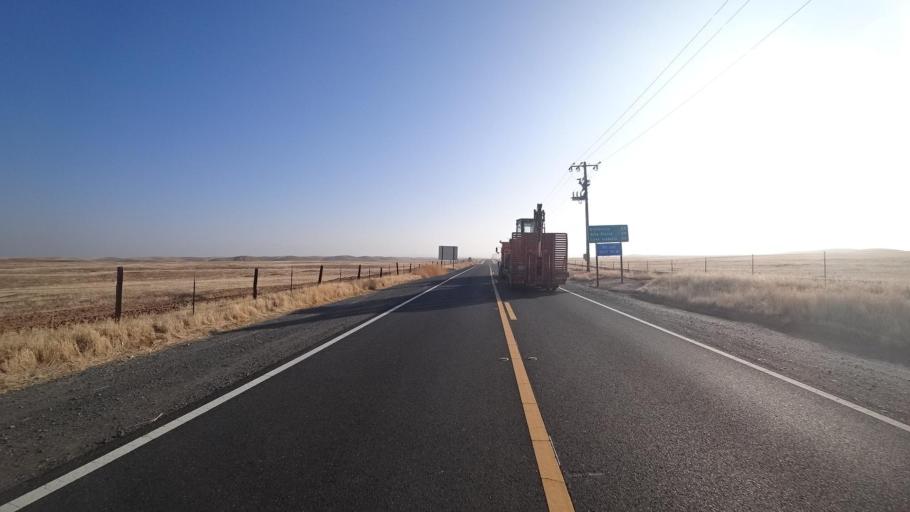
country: US
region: California
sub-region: Tulare County
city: Richgrove
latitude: 35.7620
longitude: -119.0521
